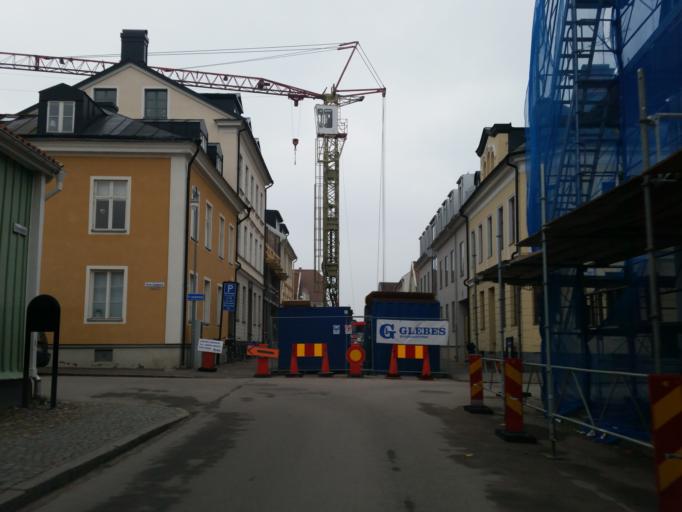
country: SE
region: Kalmar
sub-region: Kalmar Kommun
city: Kalmar
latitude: 56.6656
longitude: 16.3676
